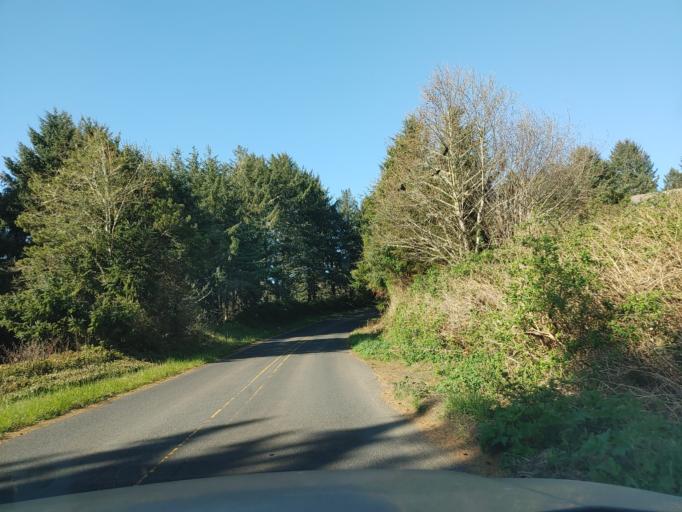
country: US
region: Oregon
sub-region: Lincoln County
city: Depoe Bay
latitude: 44.7609
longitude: -124.0654
